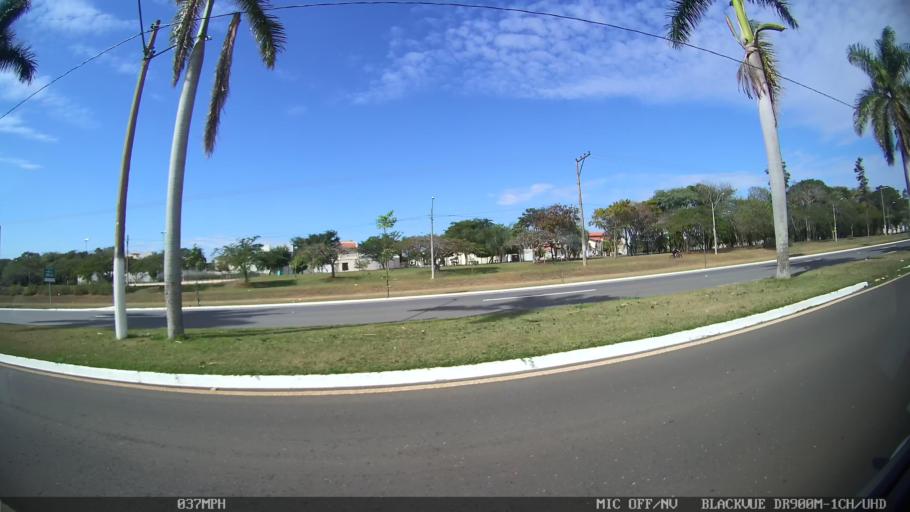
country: BR
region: Sao Paulo
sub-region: Santa Barbara D'Oeste
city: Santa Barbara d'Oeste
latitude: -22.7620
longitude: -47.4332
